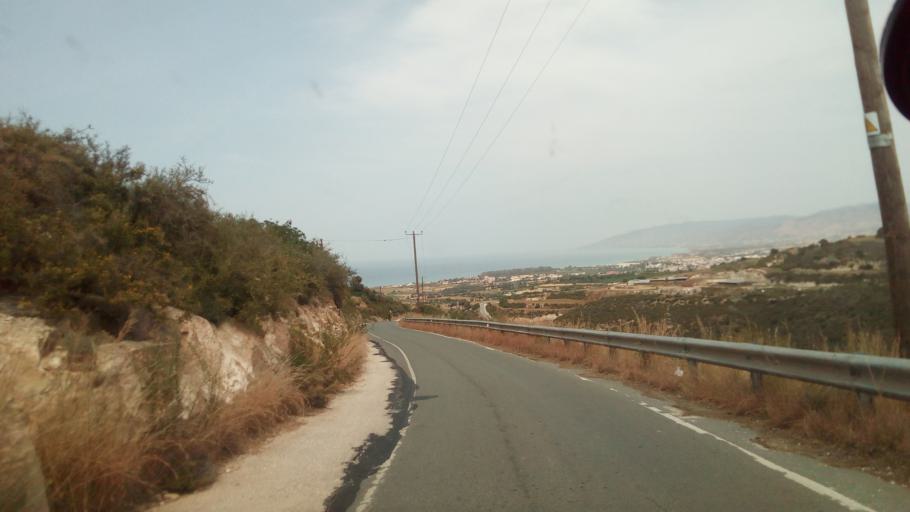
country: CY
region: Pafos
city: Polis
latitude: 35.0142
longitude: 32.3953
